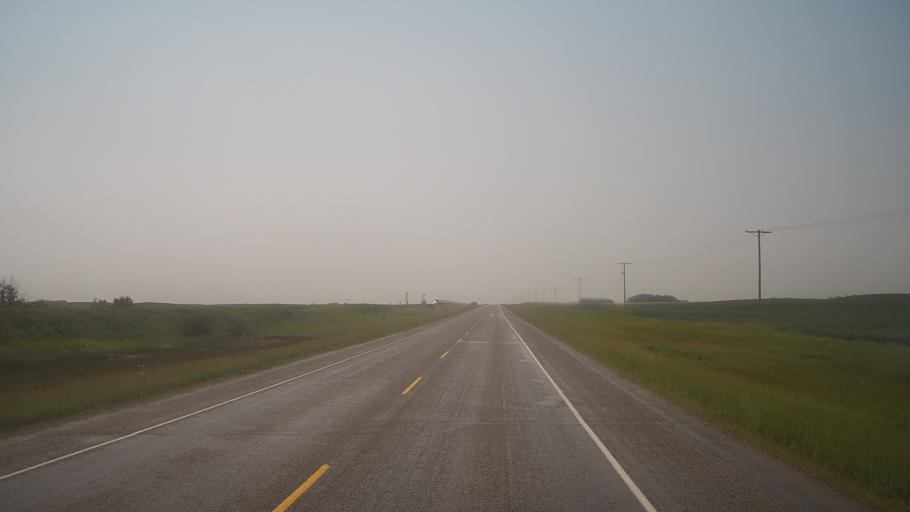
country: CA
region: Saskatchewan
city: Biggar
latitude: 52.1556
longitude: -108.2549
